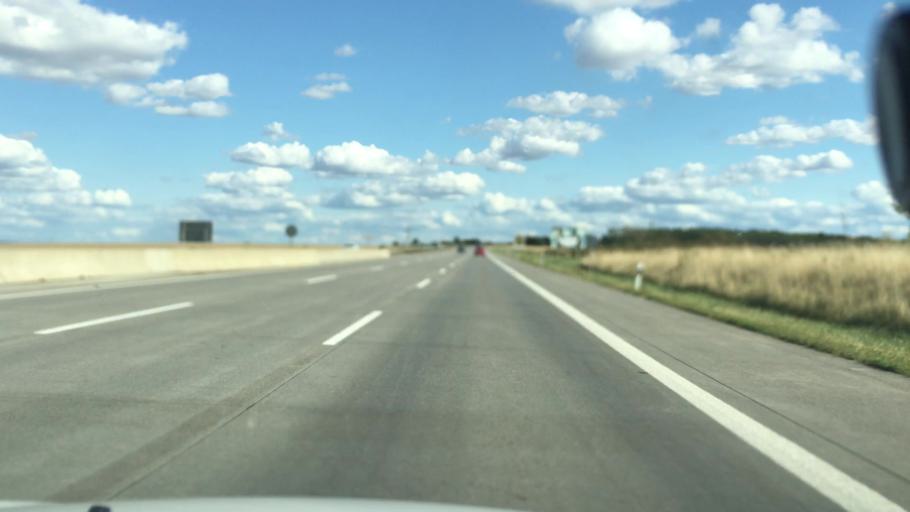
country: DE
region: Thuringia
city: Heyersdorf
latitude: 50.8410
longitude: 12.3549
